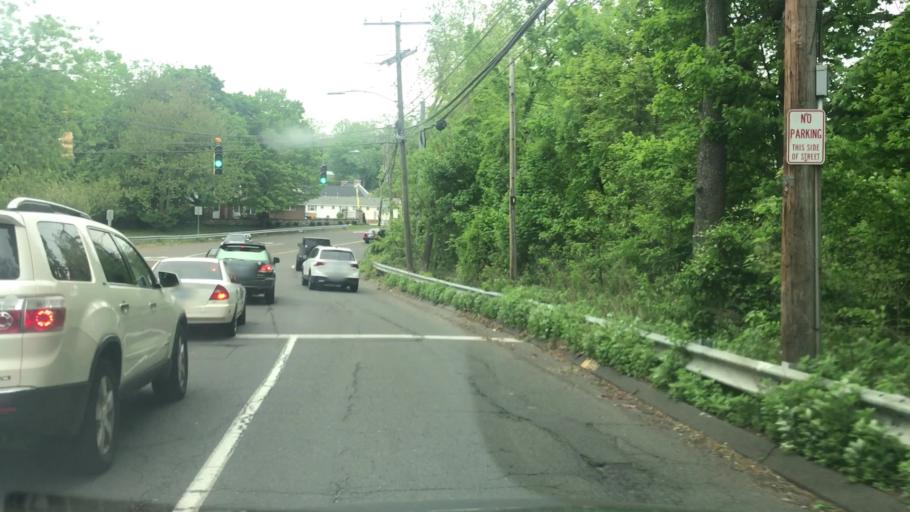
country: US
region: Connecticut
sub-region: Fairfield County
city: Stamford
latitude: 41.0571
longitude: -73.5586
